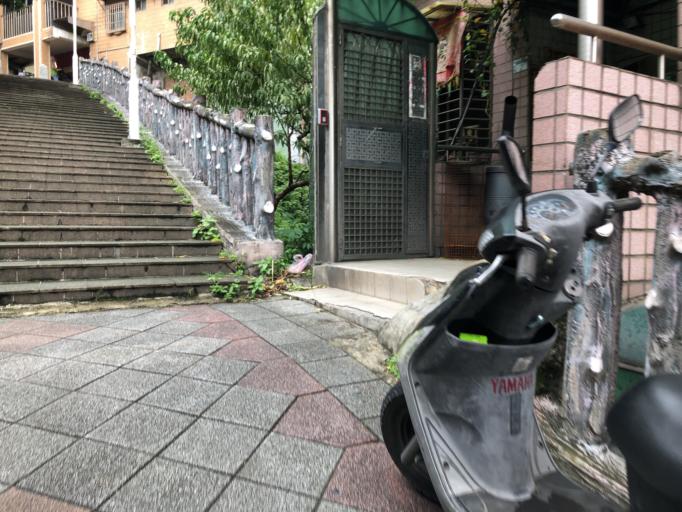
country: TW
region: Taiwan
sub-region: Taoyuan
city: Taoyuan
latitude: 24.9506
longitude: 121.3510
